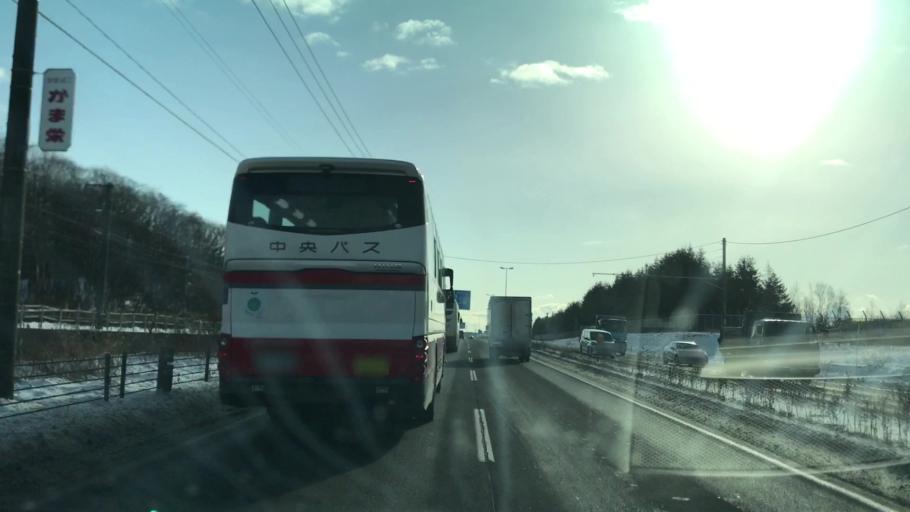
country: JP
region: Hokkaido
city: Chitose
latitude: 42.8183
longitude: 141.6629
